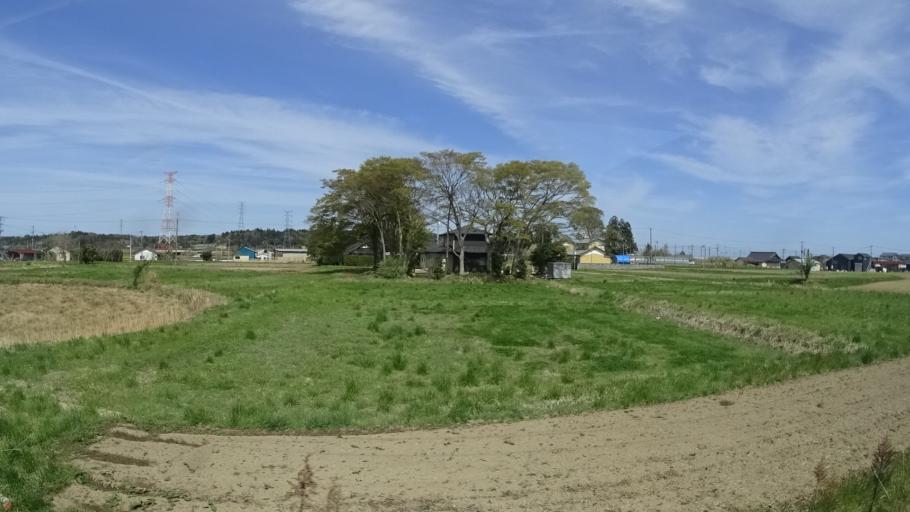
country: JP
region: Fukushima
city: Namie
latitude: 37.5927
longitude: 140.9995
